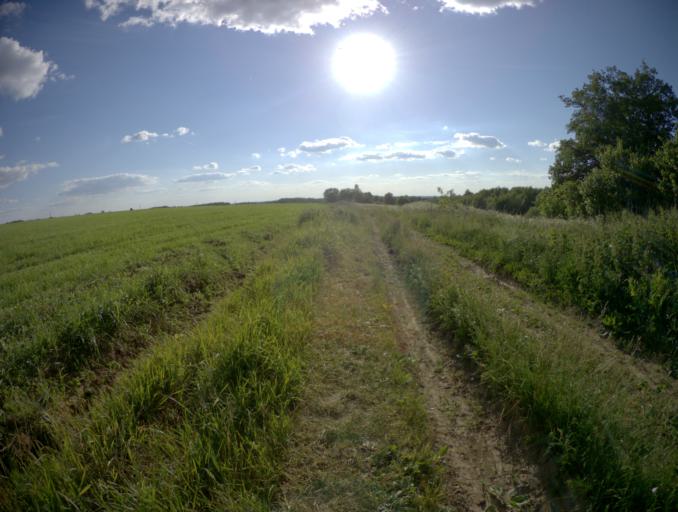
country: RU
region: Vladimir
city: Stavrovo
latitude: 56.2448
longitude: 40.0984
